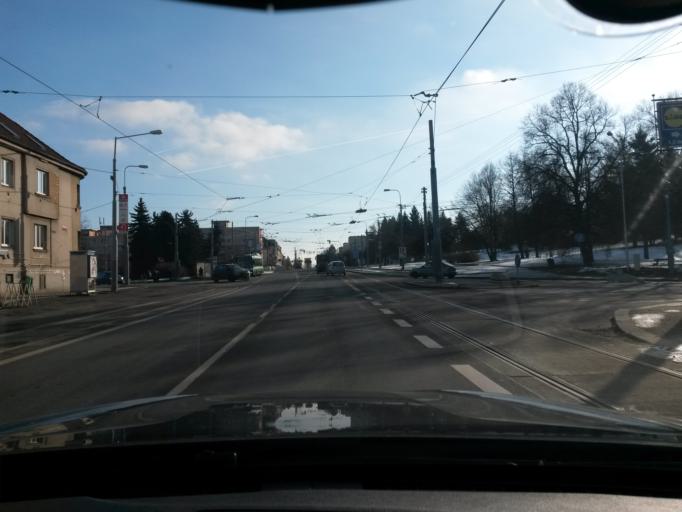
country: CZ
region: Plzensky
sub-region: Okres Plzen-Mesto
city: Pilsen
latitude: 49.7252
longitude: 13.3990
